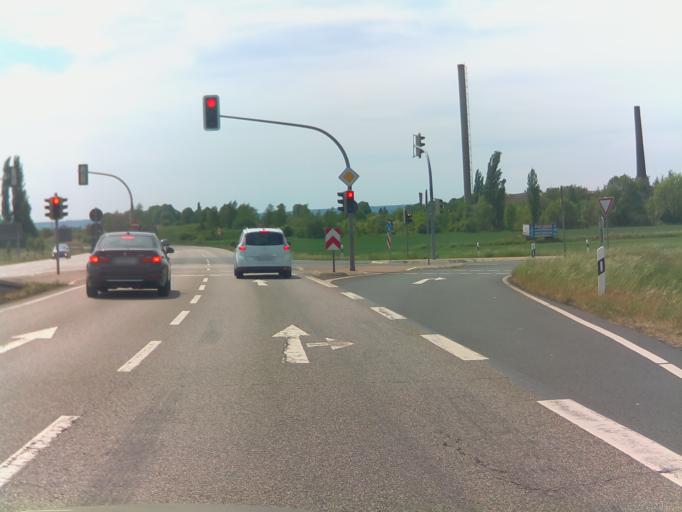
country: DE
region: Saxony-Anhalt
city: Egeln
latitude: 51.9623
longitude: 11.4483
